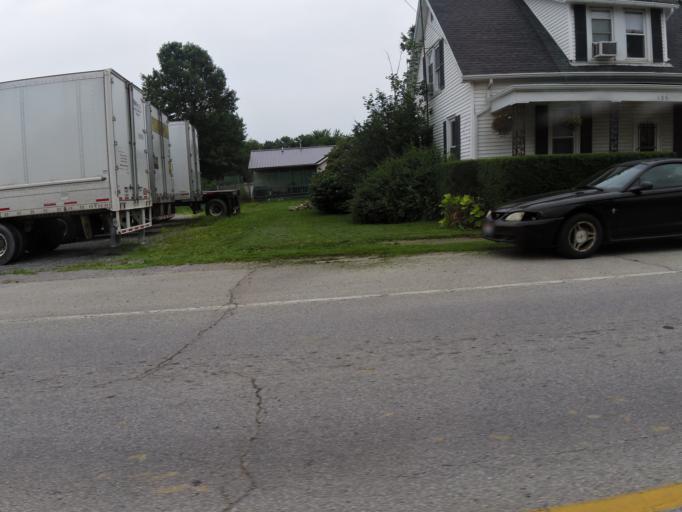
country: US
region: Ohio
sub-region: Clinton County
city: Blanchester
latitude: 39.1859
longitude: -83.9324
